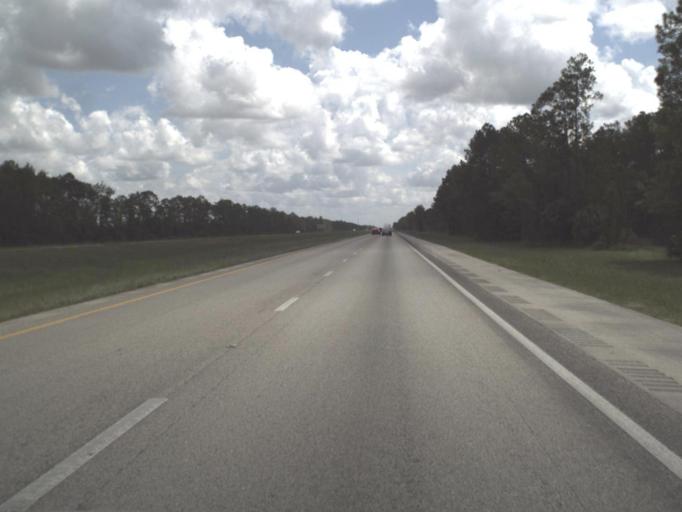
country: US
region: Florida
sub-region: Collier County
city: Golden Gate
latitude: 26.1546
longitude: -81.6408
